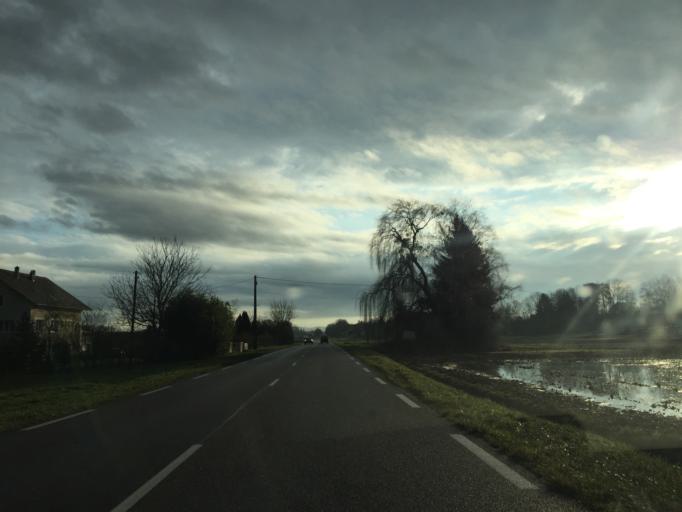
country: FR
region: Franche-Comte
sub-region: Departement du Jura
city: Mont-sous-Vaudrey
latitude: 46.9868
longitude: 5.5794
